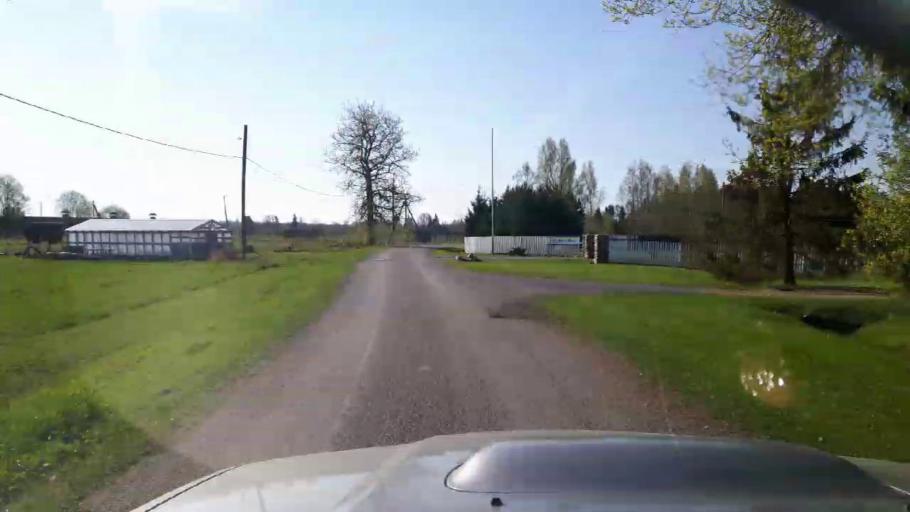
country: EE
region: Paernumaa
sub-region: Tootsi vald
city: Tootsi
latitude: 58.4884
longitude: 24.9068
